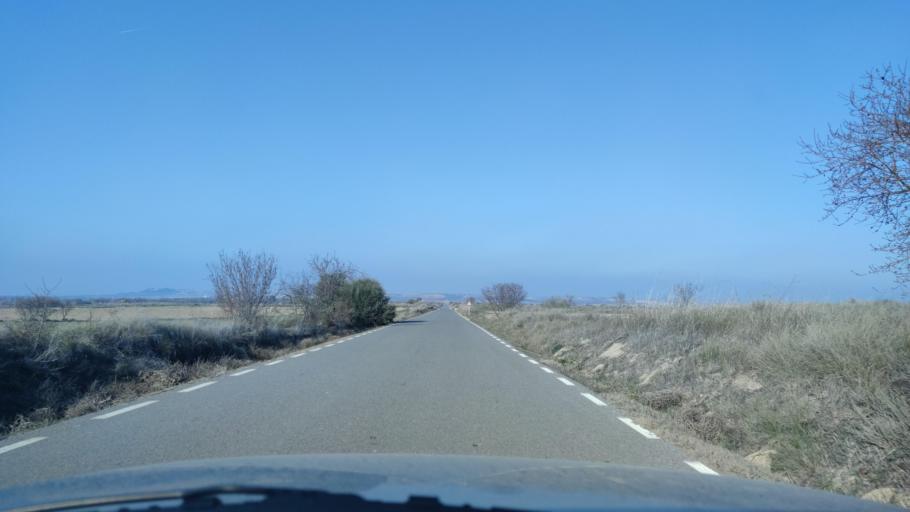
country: ES
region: Catalonia
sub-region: Provincia de Lleida
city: Sunyer
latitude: 41.4860
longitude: 0.5603
